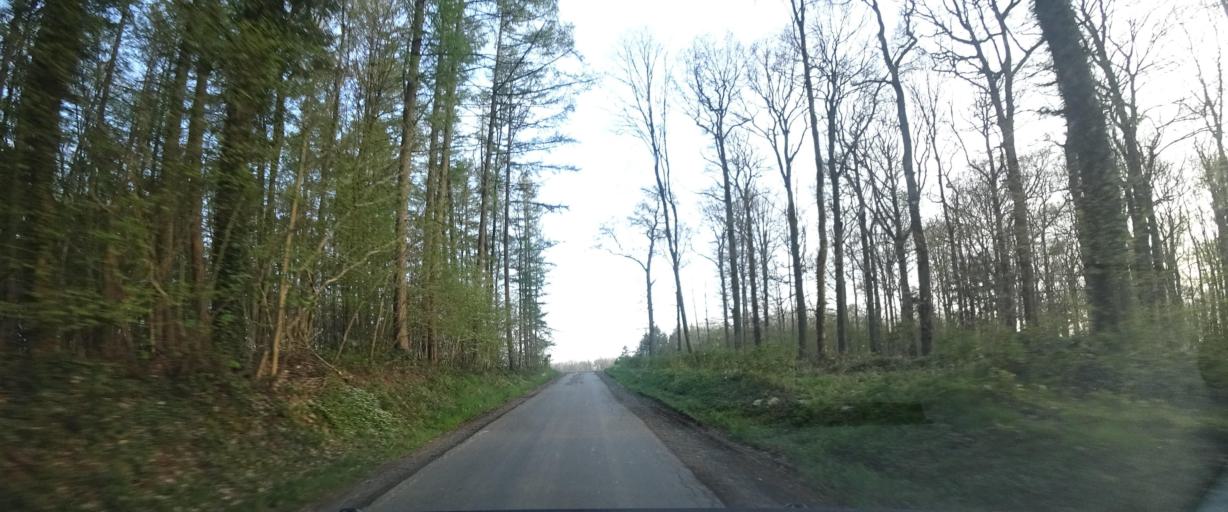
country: BE
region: Wallonia
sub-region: Province de Namur
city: Hamois
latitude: 50.3103
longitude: 5.1564
